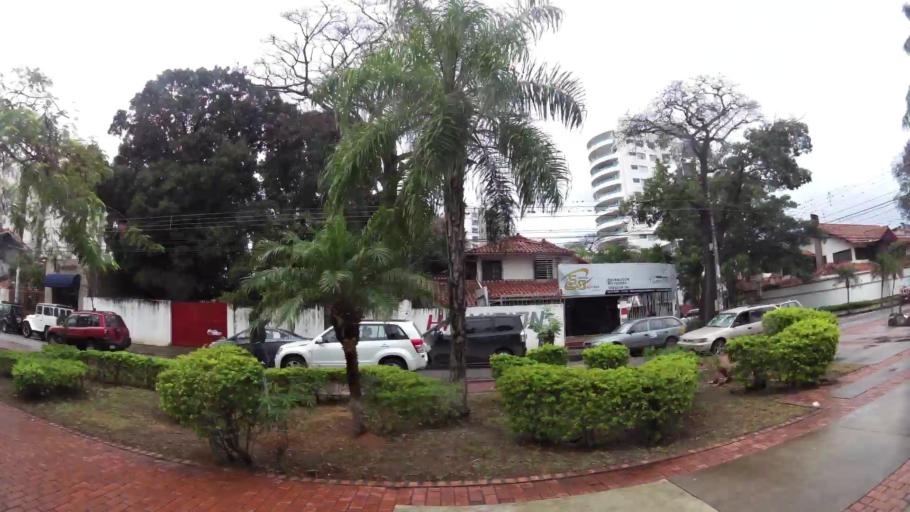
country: BO
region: Santa Cruz
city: Santa Cruz de la Sierra
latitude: -17.7929
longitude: -63.1776
